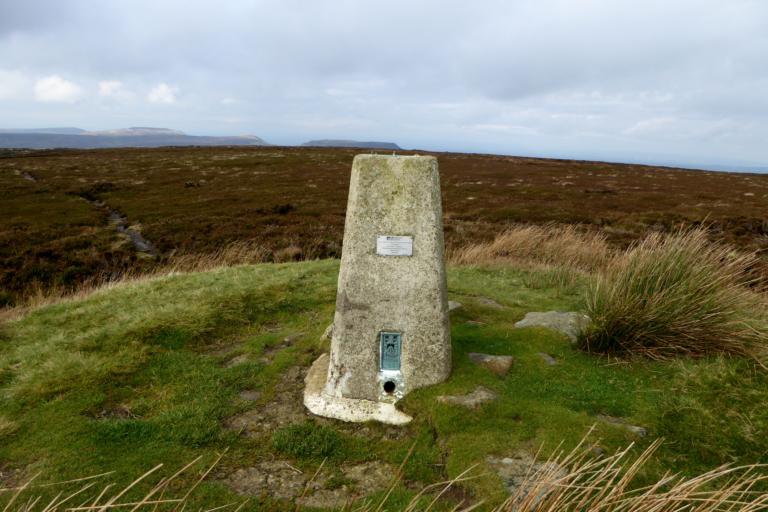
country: GB
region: England
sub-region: North Yorkshire
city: Bilsdale
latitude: 54.4063
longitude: -1.0860
